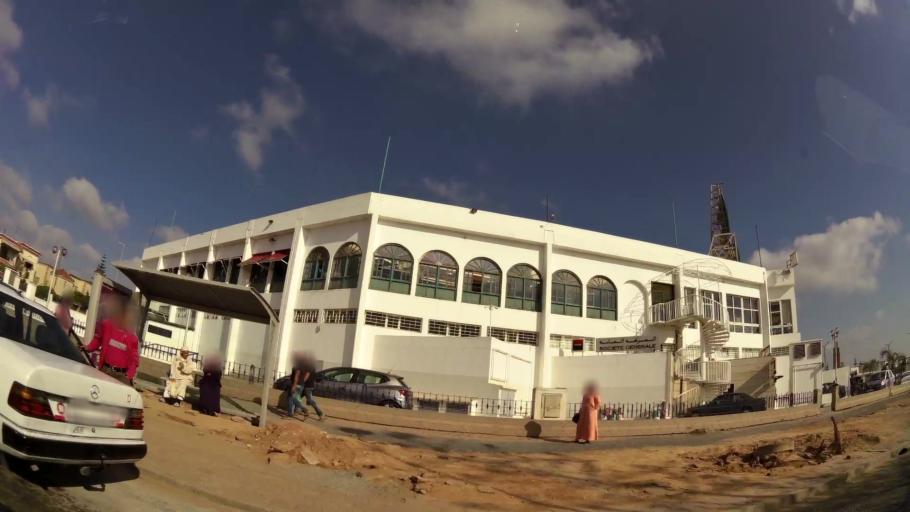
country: MA
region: Rabat-Sale-Zemmour-Zaer
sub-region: Skhirate-Temara
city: Temara
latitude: 33.9488
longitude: -6.8695
